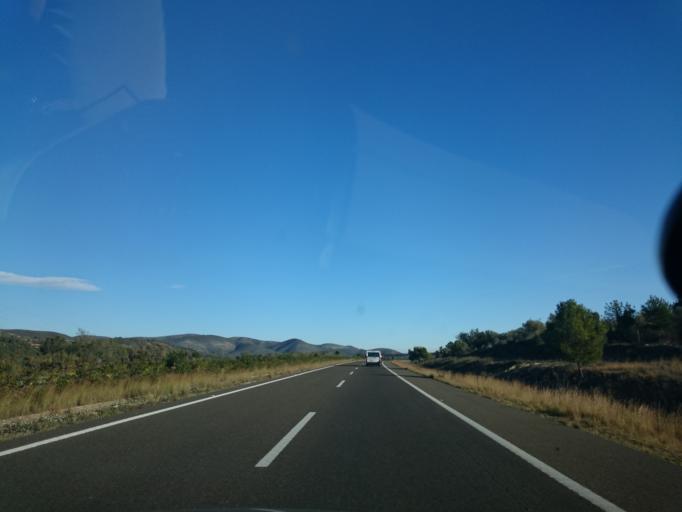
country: ES
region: Valencia
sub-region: Provincia de Castello
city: Santa Magdalena de Pulpis
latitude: 40.3380
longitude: 0.2688
